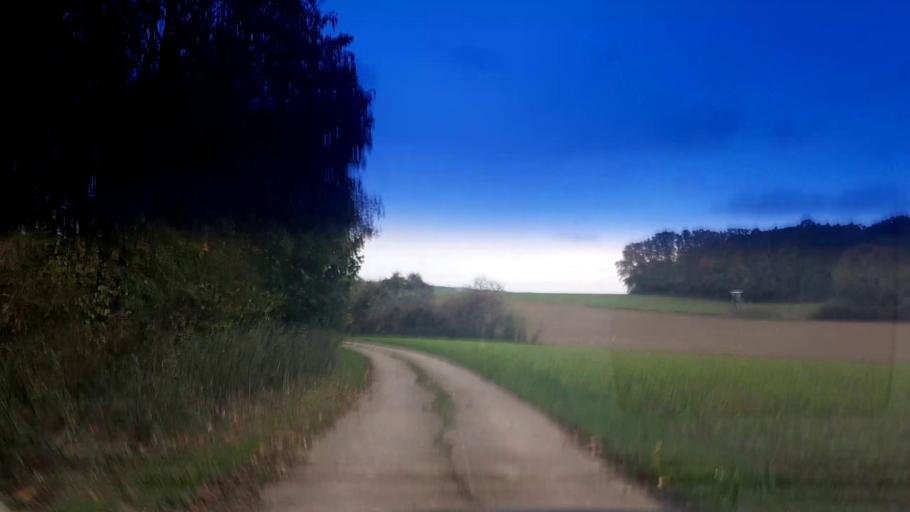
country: DE
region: Bavaria
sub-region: Upper Franconia
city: Memmelsdorf
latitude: 49.9673
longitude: 10.9577
